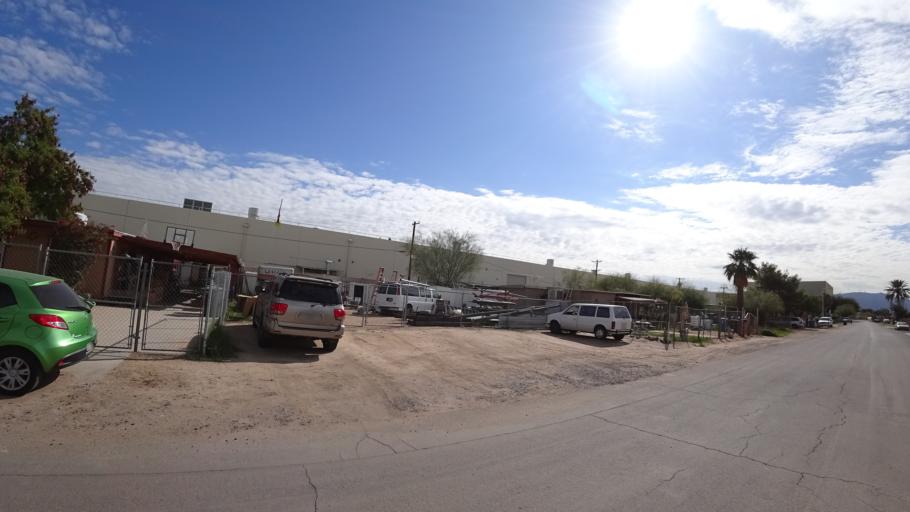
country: US
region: Arizona
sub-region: Maricopa County
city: Phoenix
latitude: 33.4162
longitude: -112.0686
